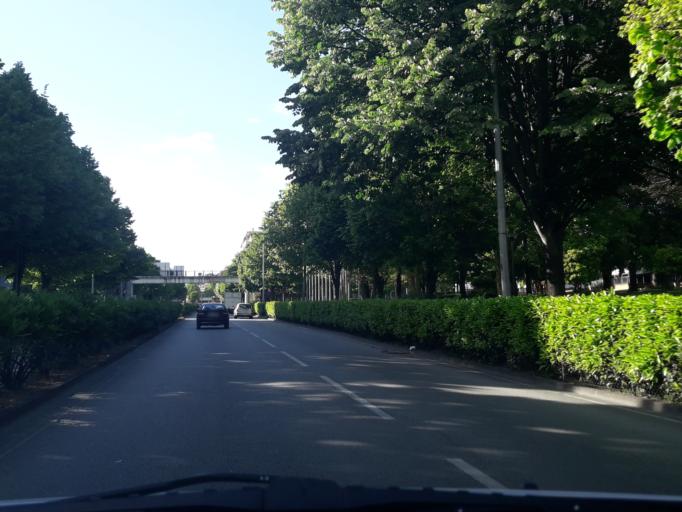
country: PT
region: Braga
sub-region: Vila Nova de Famalicao
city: Vila Nova de Famalicao
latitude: 41.4118
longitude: -8.5171
